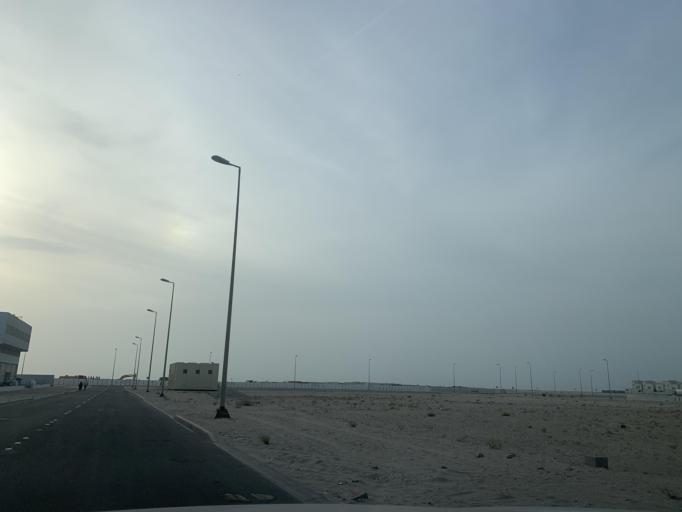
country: BH
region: Muharraq
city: Al Muharraq
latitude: 26.3098
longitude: 50.6198
